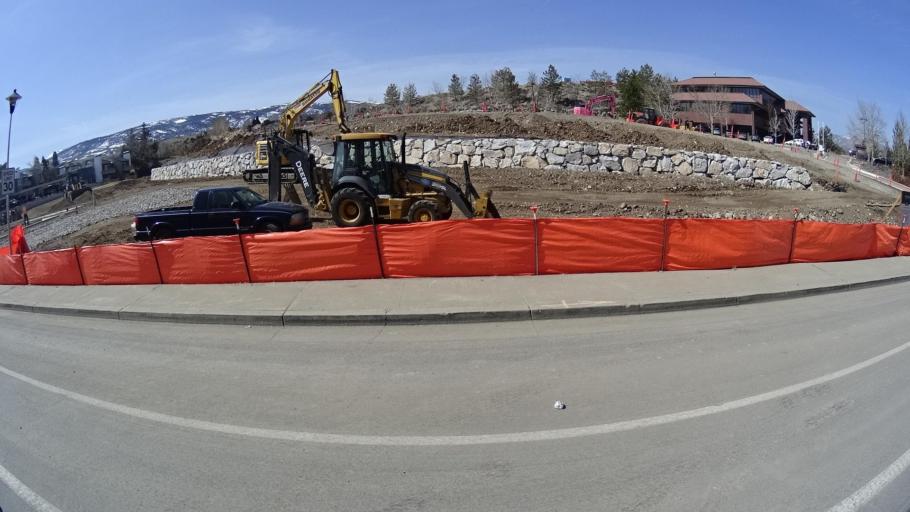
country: US
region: Nevada
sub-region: Washoe County
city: Reno
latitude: 39.4756
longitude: -119.8118
